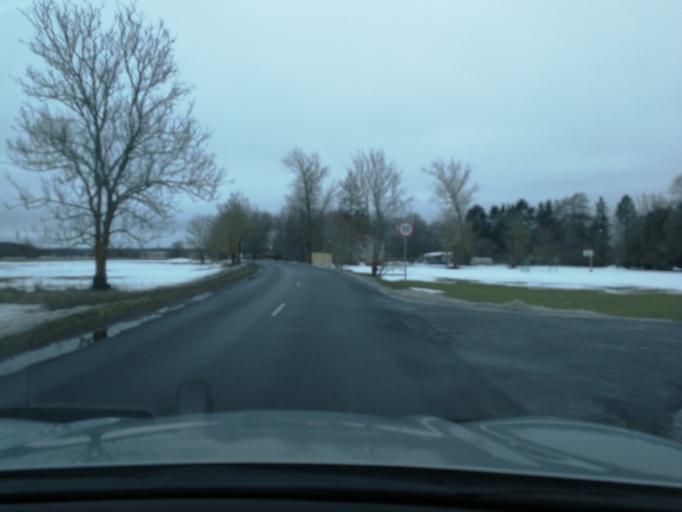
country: EE
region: Harju
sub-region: Kiili vald
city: Kiili
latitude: 59.2761
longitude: 24.8746
